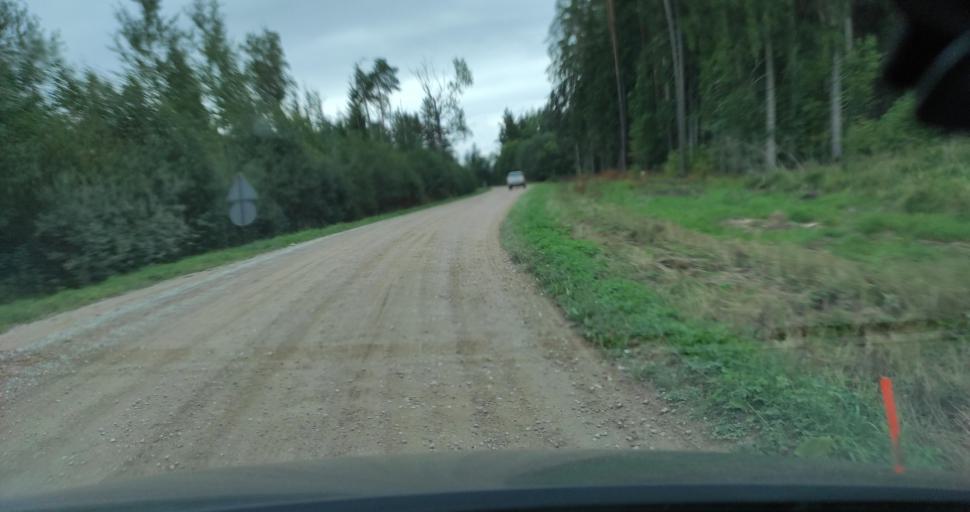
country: LV
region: Talsu Rajons
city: Stende
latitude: 57.0417
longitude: 22.3084
